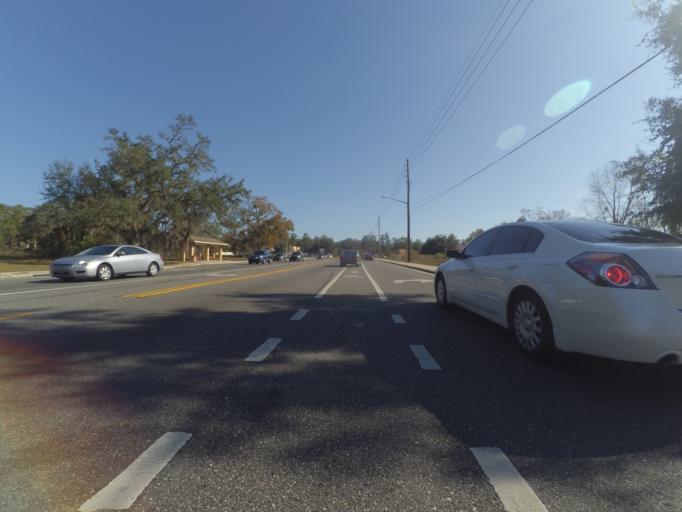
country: US
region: Florida
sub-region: Alachua County
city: Gainesville
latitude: 29.6371
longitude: -82.3907
